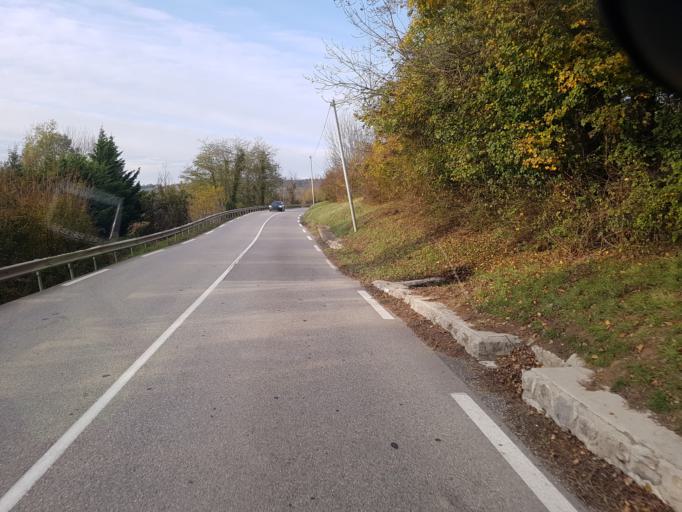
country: FR
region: Rhone-Alpes
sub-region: Departement de la Haute-Savoie
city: Frangy
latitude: 46.0446
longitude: 5.8850
